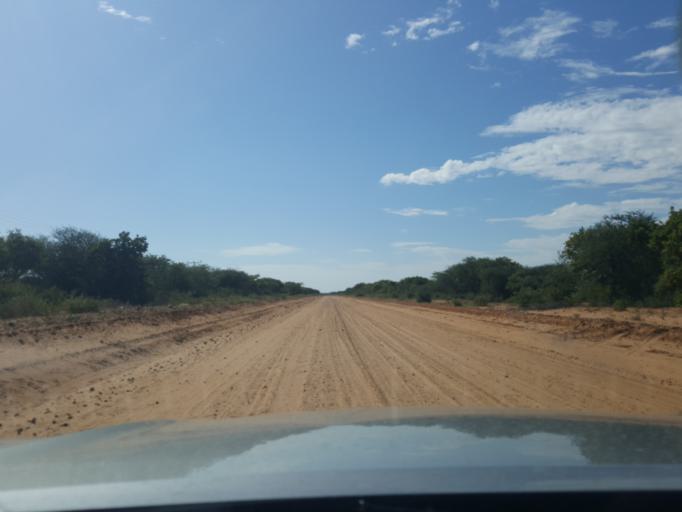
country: BW
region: Kweneng
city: Khudumelapye
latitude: -23.7196
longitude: 24.7362
